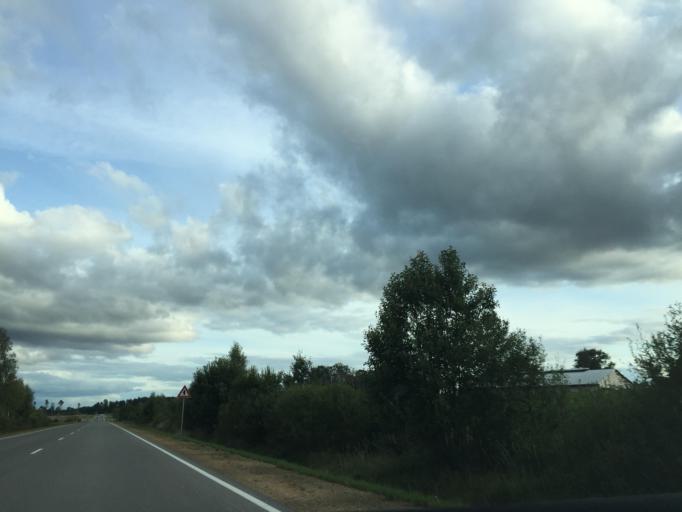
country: LV
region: Nereta
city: Nereta
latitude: 56.2344
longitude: 25.2719
